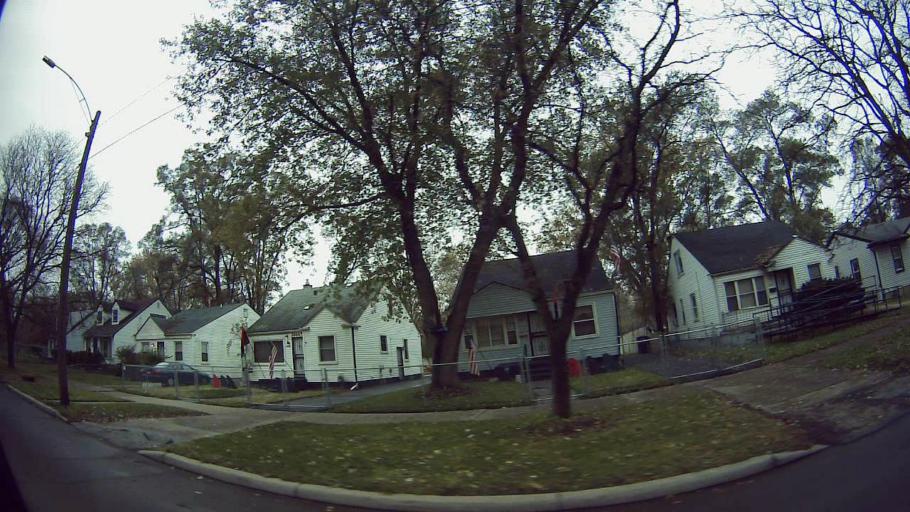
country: US
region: Michigan
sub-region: Oakland County
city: Southfield
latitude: 42.4253
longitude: -83.2387
